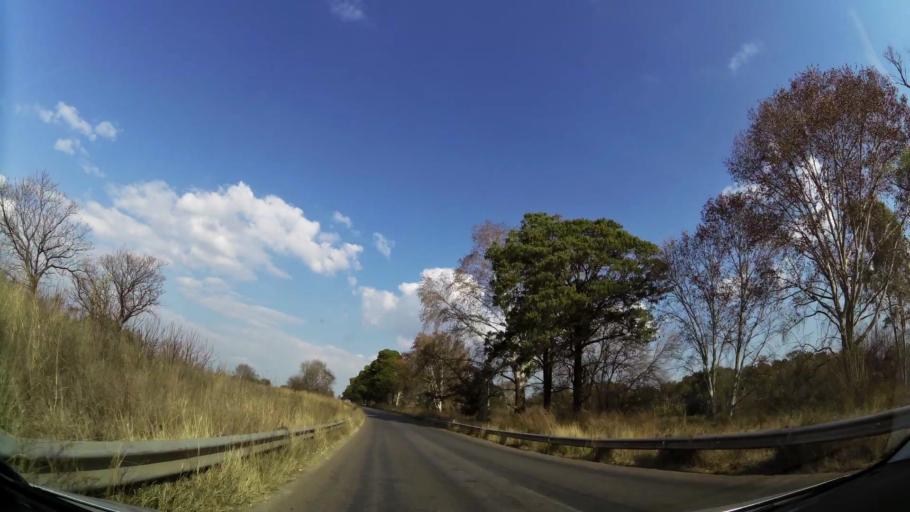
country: ZA
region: Gauteng
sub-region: Ekurhuleni Metropolitan Municipality
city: Tembisa
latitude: -25.9228
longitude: 28.2277
